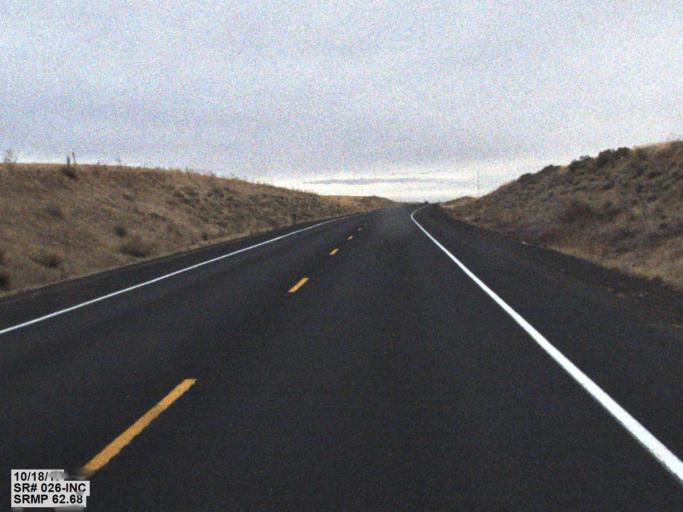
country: US
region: Washington
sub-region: Franklin County
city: Connell
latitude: 46.7944
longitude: -118.7142
